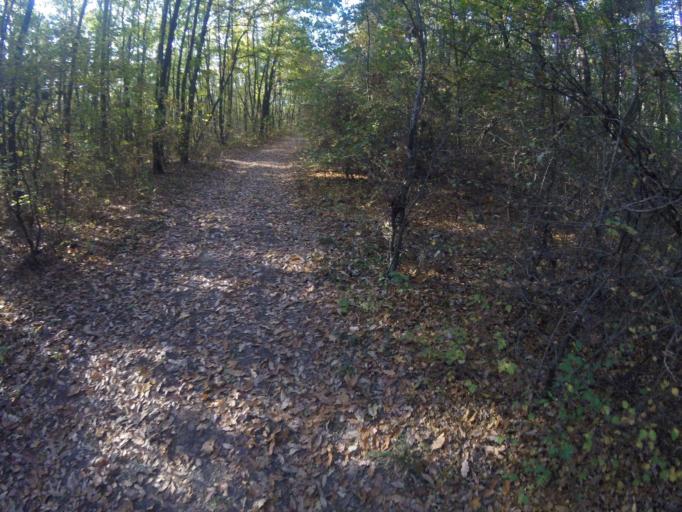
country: HU
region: Fejer
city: Bodajk
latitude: 47.3137
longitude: 18.2245
